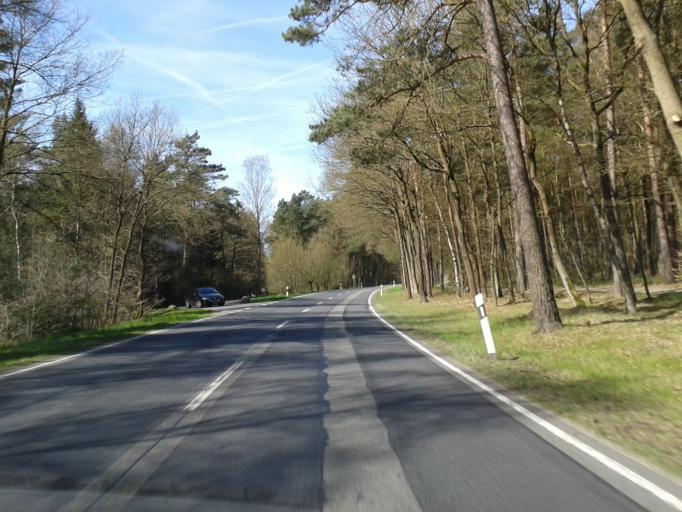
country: DE
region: Lower Saxony
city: Eimke
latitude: 52.9665
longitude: 10.3508
